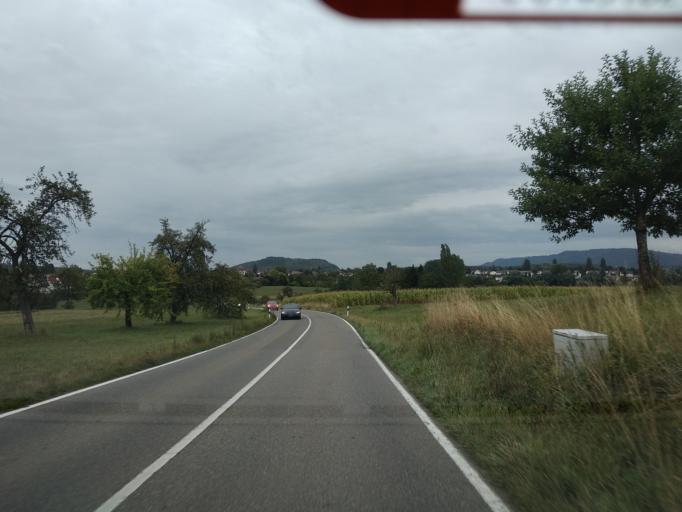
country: DE
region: Baden-Wuerttemberg
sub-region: Freiburg Region
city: Gottmadingen
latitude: 47.7319
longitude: 8.7634
